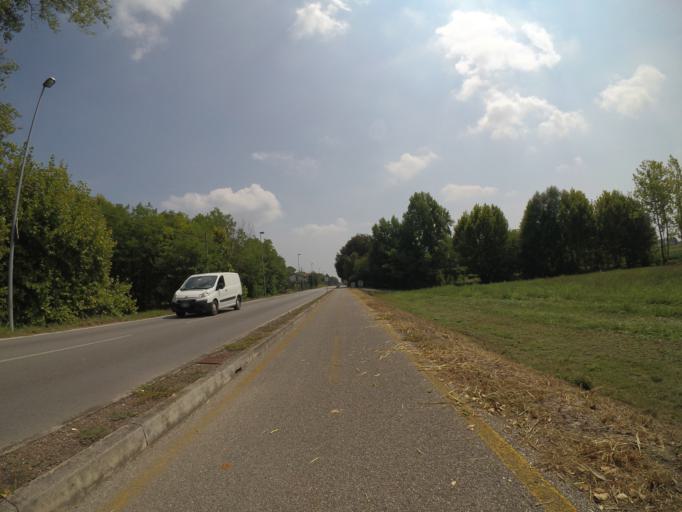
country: IT
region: Friuli Venezia Giulia
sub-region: Provincia di Udine
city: Teor
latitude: 45.8532
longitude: 13.0603
